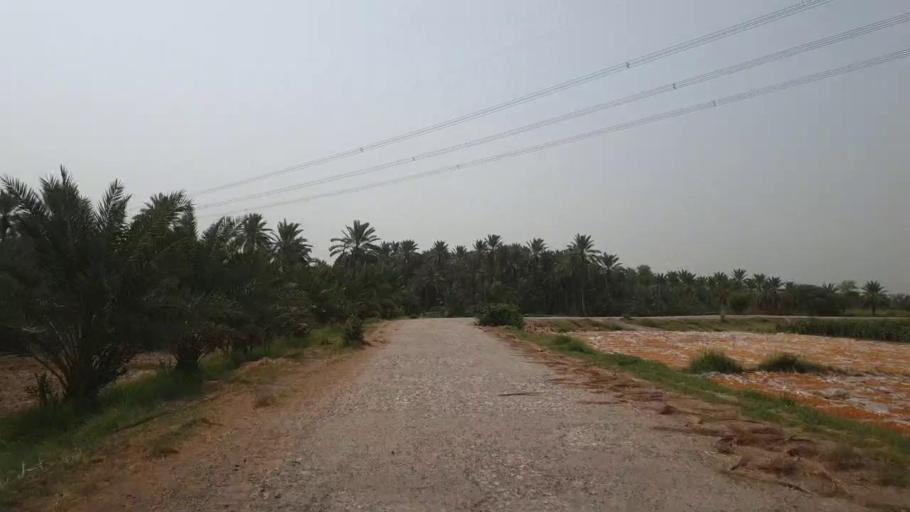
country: PK
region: Sindh
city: Gambat
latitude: 27.4134
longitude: 68.5539
